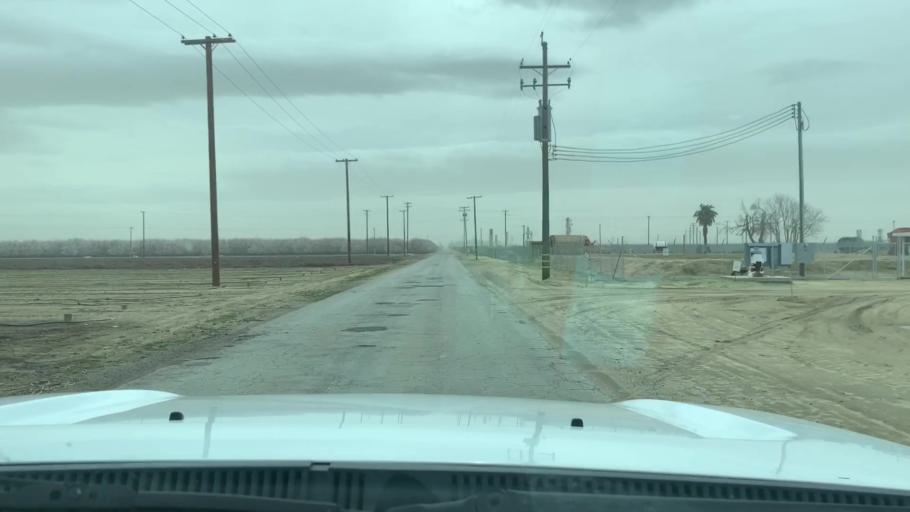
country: US
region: California
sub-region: Kern County
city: Shafter
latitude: 35.5313
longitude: -119.2689
